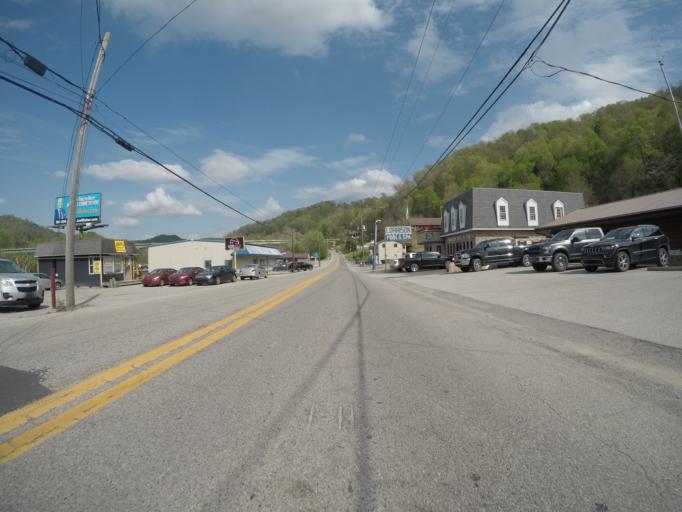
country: US
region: West Virginia
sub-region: Boone County
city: Madison
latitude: 38.0830
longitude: -81.8355
